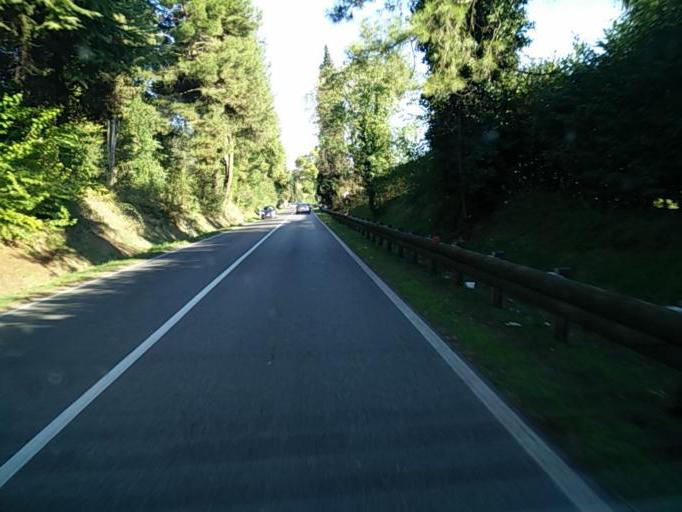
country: IT
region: Lombardy
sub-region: Provincia di Brescia
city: Salo
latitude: 45.6109
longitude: 10.5158
